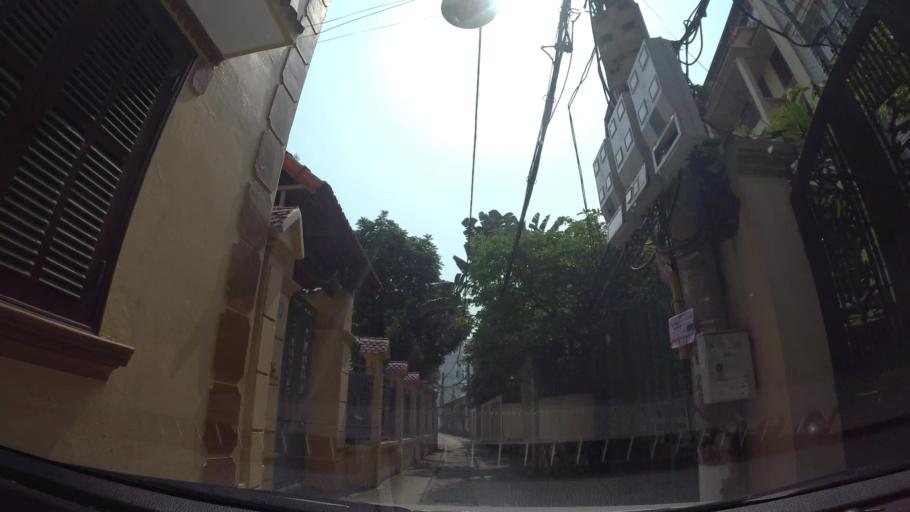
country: VN
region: Ha Noi
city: Tay Ho
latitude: 21.0871
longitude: 105.8137
